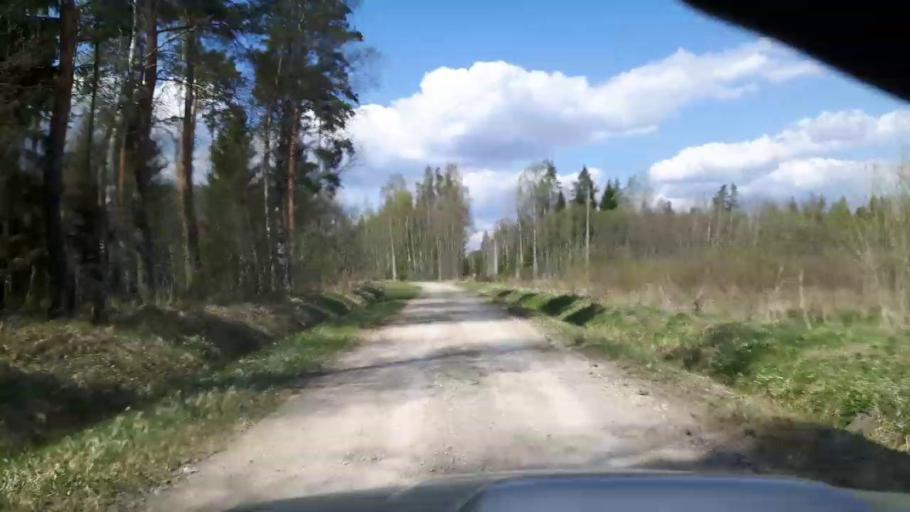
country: EE
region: Paernumaa
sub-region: Tootsi vald
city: Tootsi
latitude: 58.4526
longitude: 24.8938
